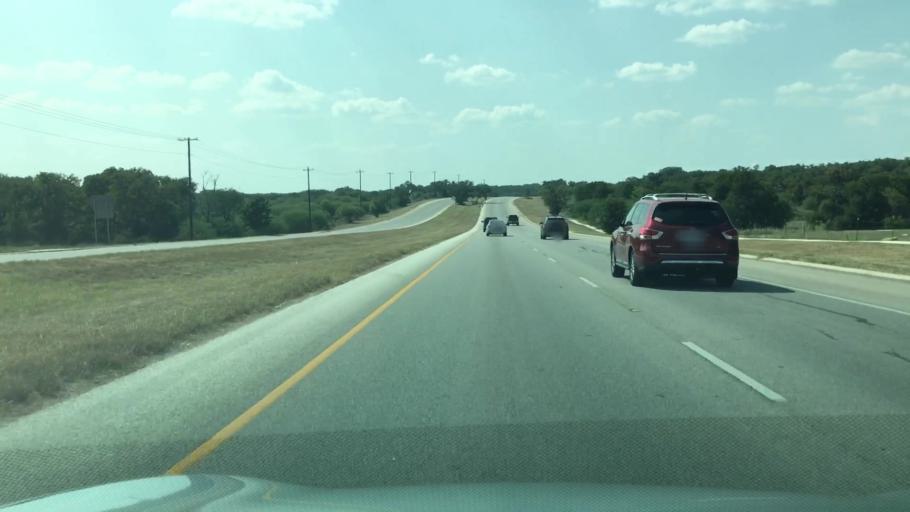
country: US
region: Texas
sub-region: Hays County
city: San Marcos
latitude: 29.8818
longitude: -97.9733
